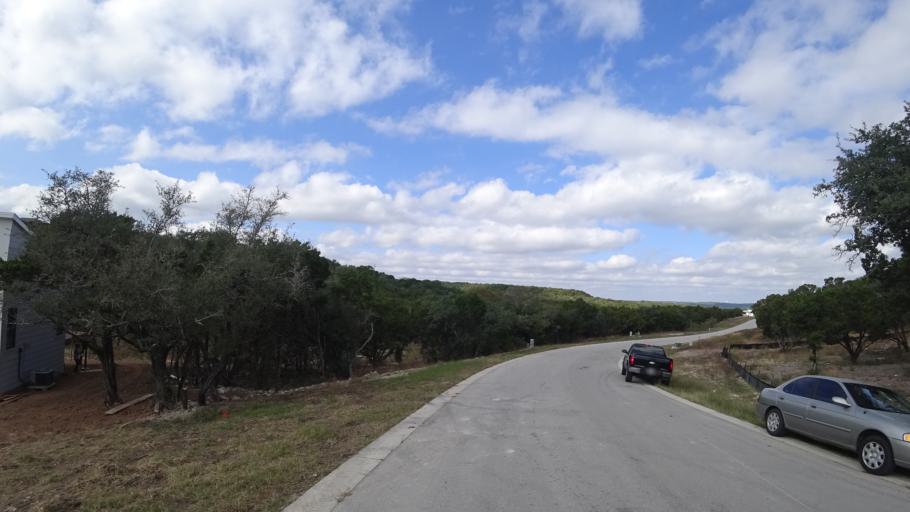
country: US
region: Texas
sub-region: Travis County
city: Bee Cave
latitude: 30.2535
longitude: -97.9272
